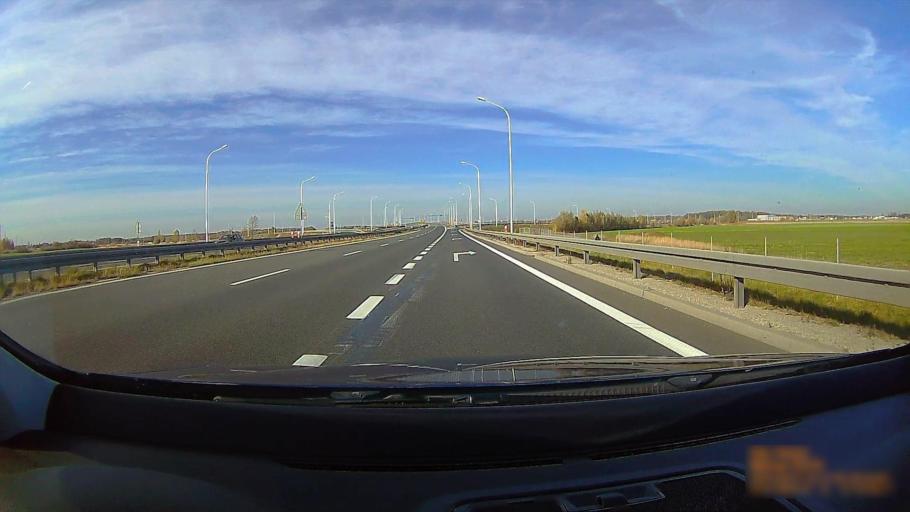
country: PL
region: Greater Poland Voivodeship
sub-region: Powiat ostrowski
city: Ostrow Wielkopolski
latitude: 51.6617
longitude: 17.8596
